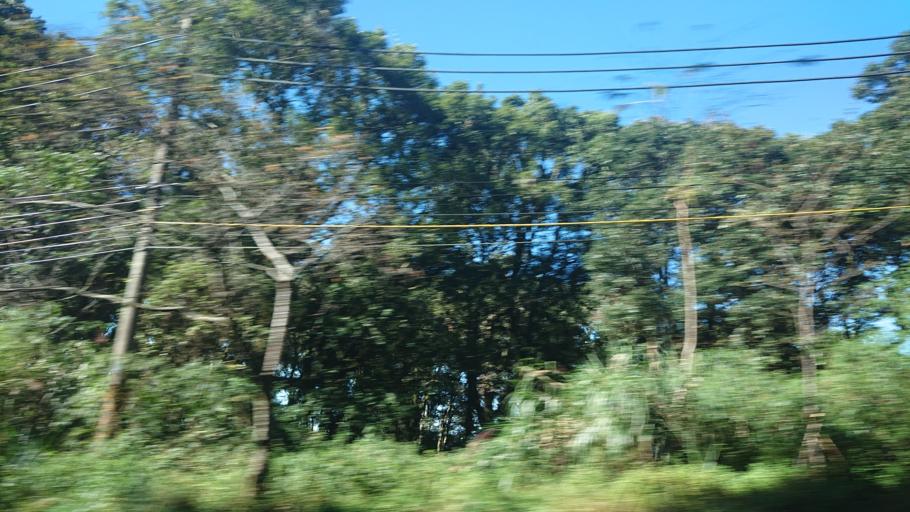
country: TW
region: Taiwan
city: Lugu
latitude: 23.4975
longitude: 120.7977
